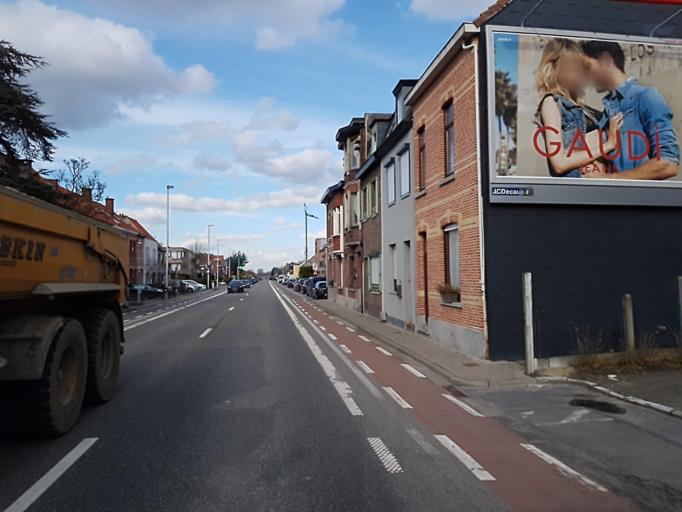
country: BE
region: Flanders
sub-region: Provincie Oost-Vlaanderen
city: Sint-Niklaas
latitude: 51.1785
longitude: 4.1545
